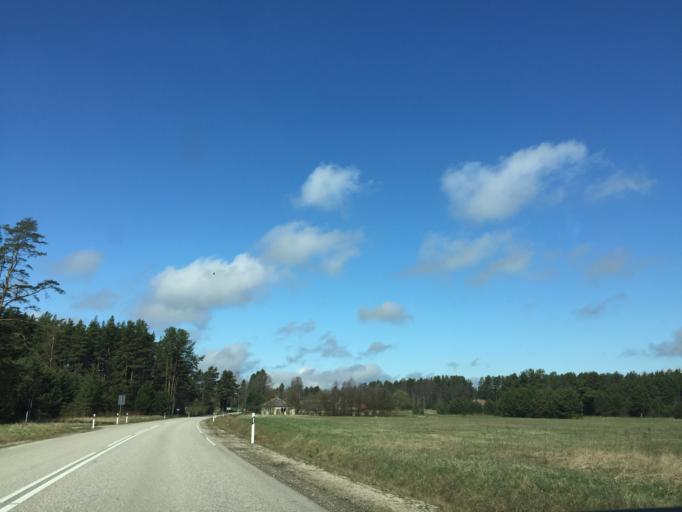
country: LV
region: Apes Novads
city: Ape
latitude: 57.5370
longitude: 26.7181
